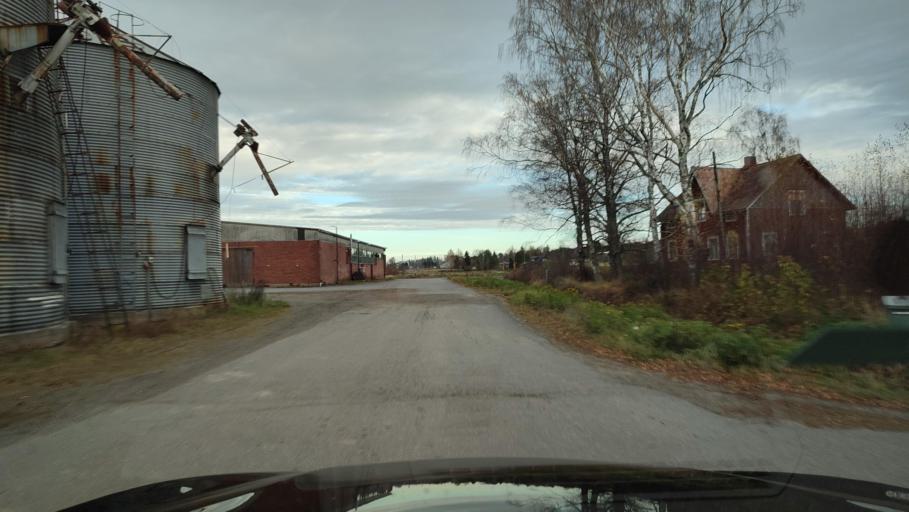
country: FI
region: Ostrobothnia
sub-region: Sydosterbotten
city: Naerpes
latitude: 62.4658
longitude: 21.3601
